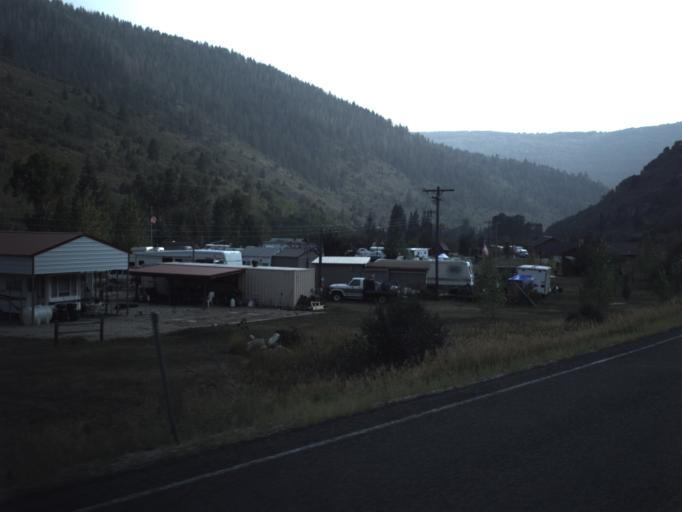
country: US
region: Utah
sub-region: Summit County
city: Francis
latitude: 40.6258
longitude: -111.2036
